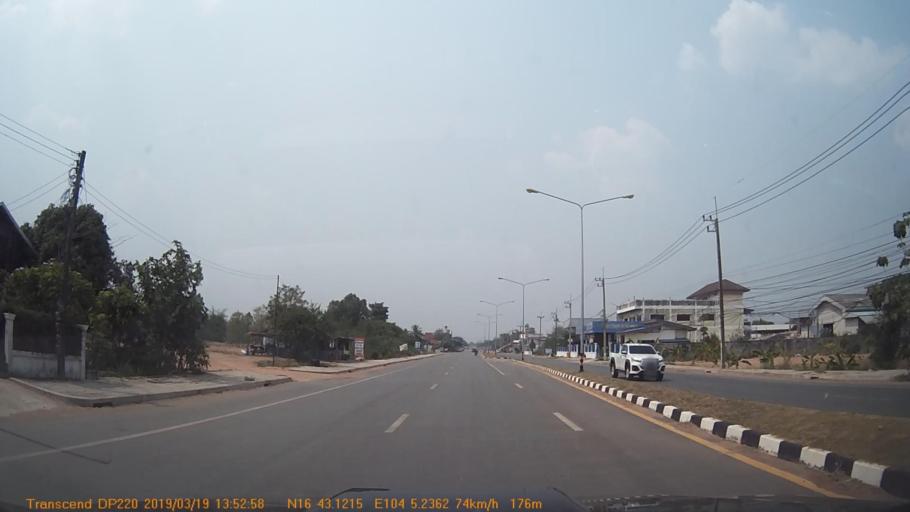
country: TH
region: Kalasin
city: Khao Wong
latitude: 16.7191
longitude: 104.0871
